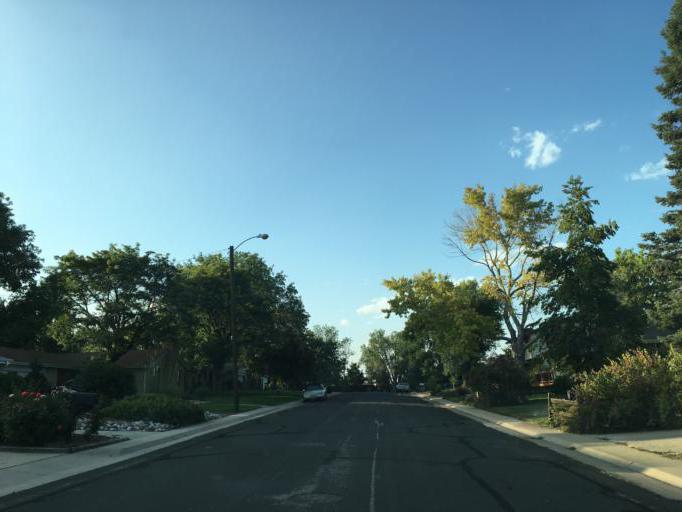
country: US
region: Colorado
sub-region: Jefferson County
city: Applewood
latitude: 39.7928
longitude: -105.1484
